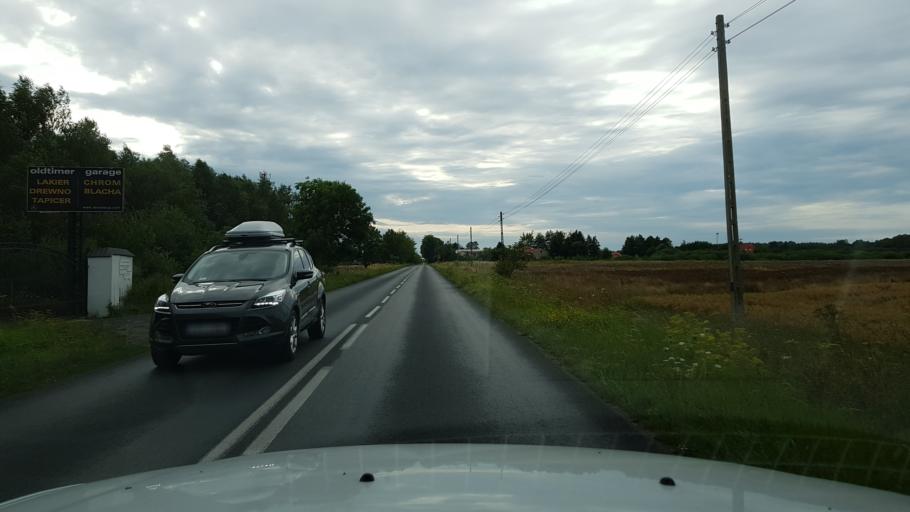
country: PL
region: West Pomeranian Voivodeship
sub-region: Powiat kolobrzeski
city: Dygowo
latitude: 54.1412
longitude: 15.6977
